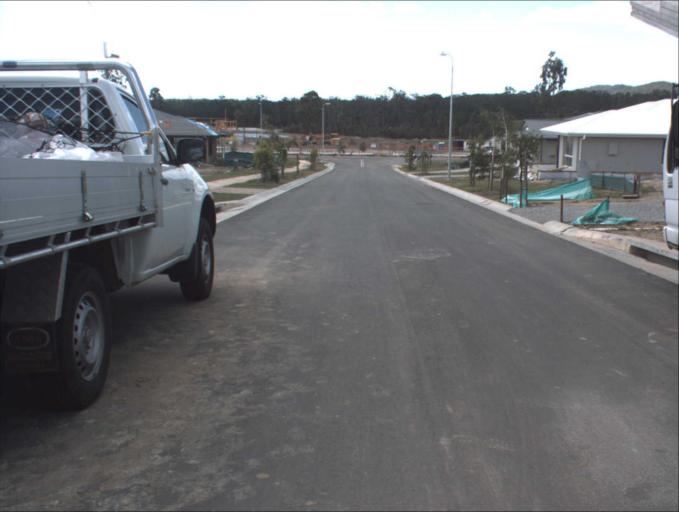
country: AU
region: Queensland
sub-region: Logan
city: Chambers Flat
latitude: -27.8019
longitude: 153.1154
